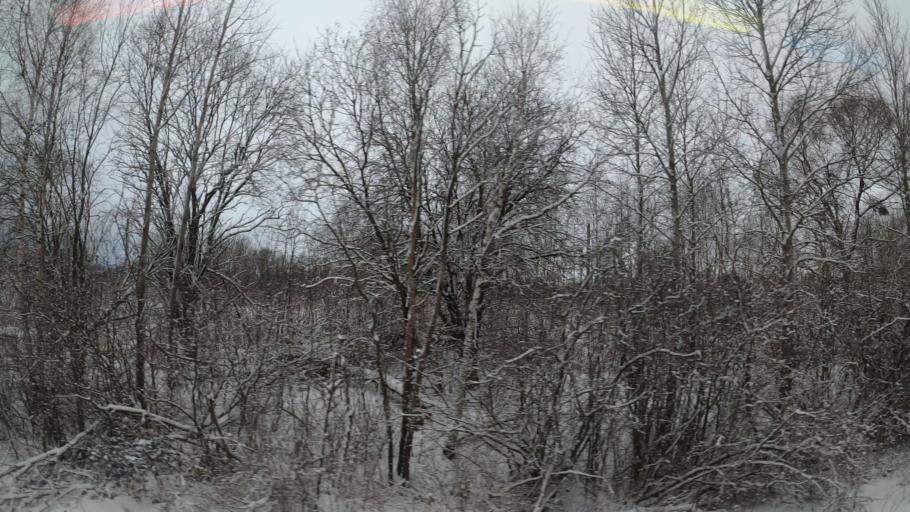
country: RU
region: Jaroslavl
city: Pereslavl'-Zalesskiy
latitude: 56.7298
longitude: 38.9018
